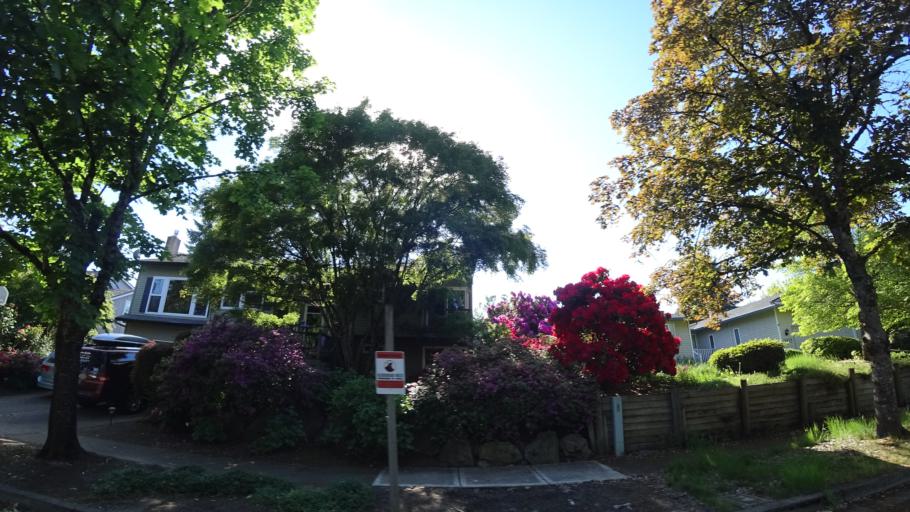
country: US
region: Oregon
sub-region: Washington County
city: Beaverton
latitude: 45.4560
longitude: -122.8062
